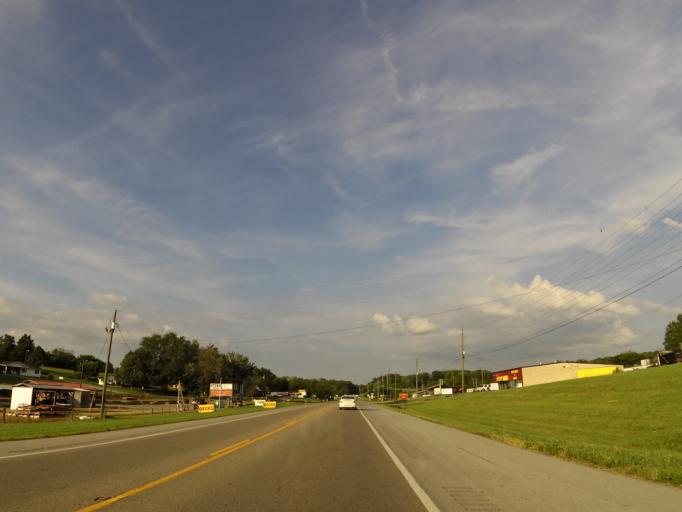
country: US
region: Tennessee
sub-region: Sevier County
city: Sevierville
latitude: 35.8776
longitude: -83.4824
